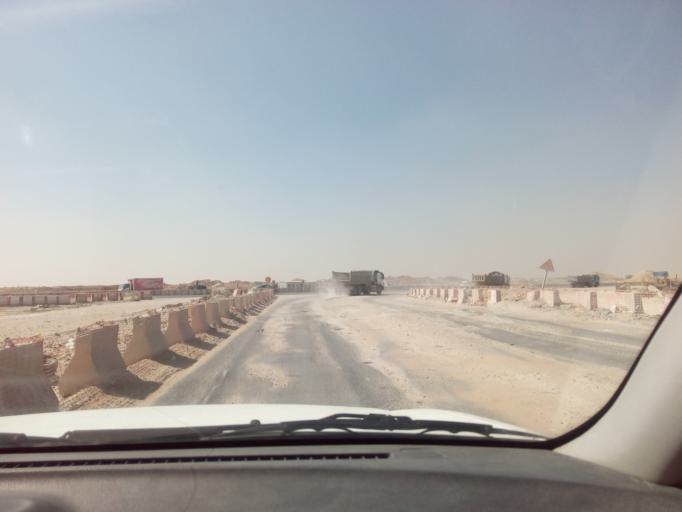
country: SA
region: Ar Riyad
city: Riyadh
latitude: 24.6358
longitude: 46.8739
